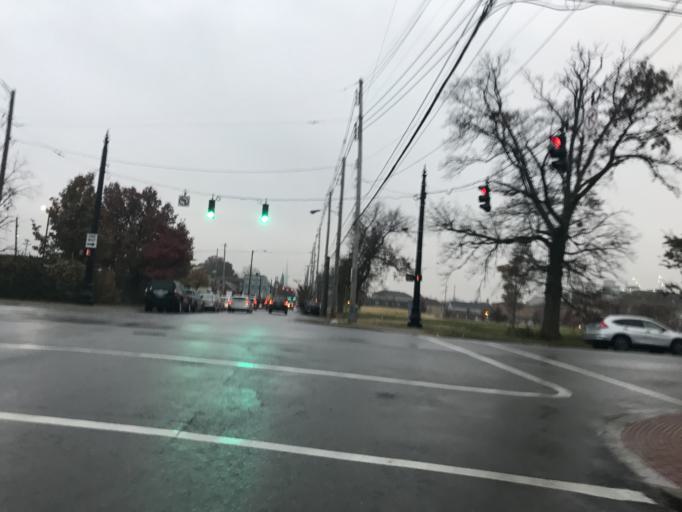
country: US
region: Kentucky
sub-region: Jefferson County
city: Louisville
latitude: 38.2520
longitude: -85.7383
